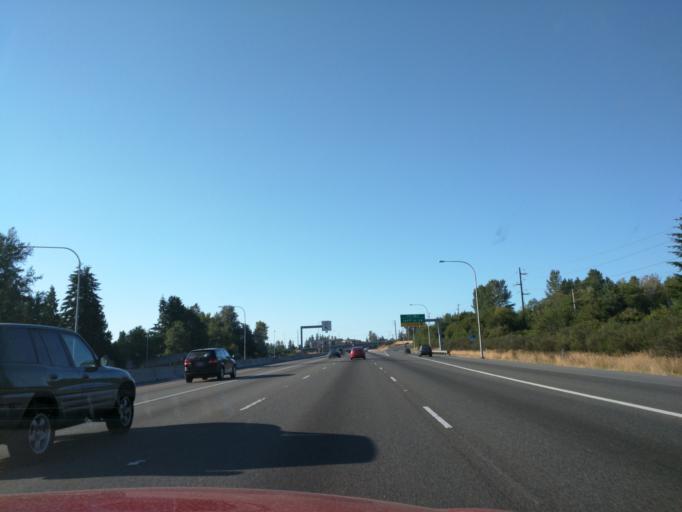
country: US
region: Washington
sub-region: Snohomish County
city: Martha Lake
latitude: 47.8438
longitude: -122.2588
